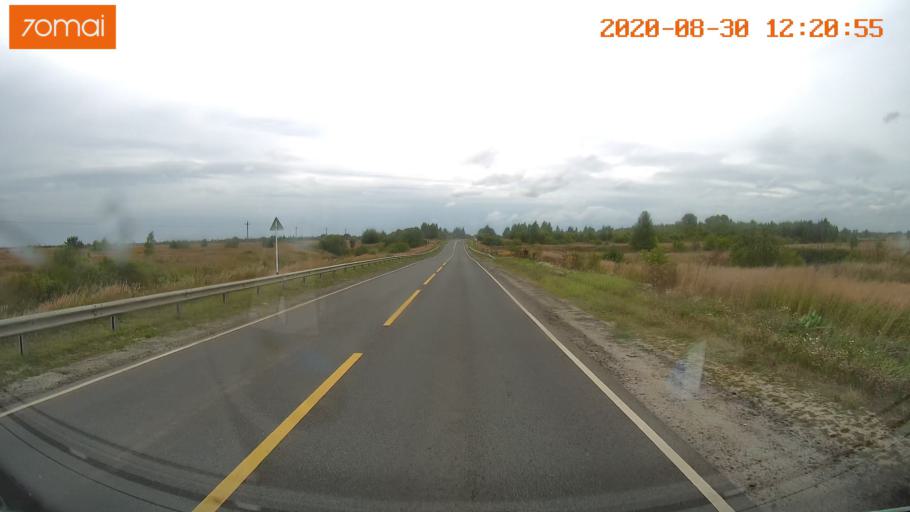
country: RU
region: Ivanovo
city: Yur'yevets
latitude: 57.3237
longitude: 42.8885
